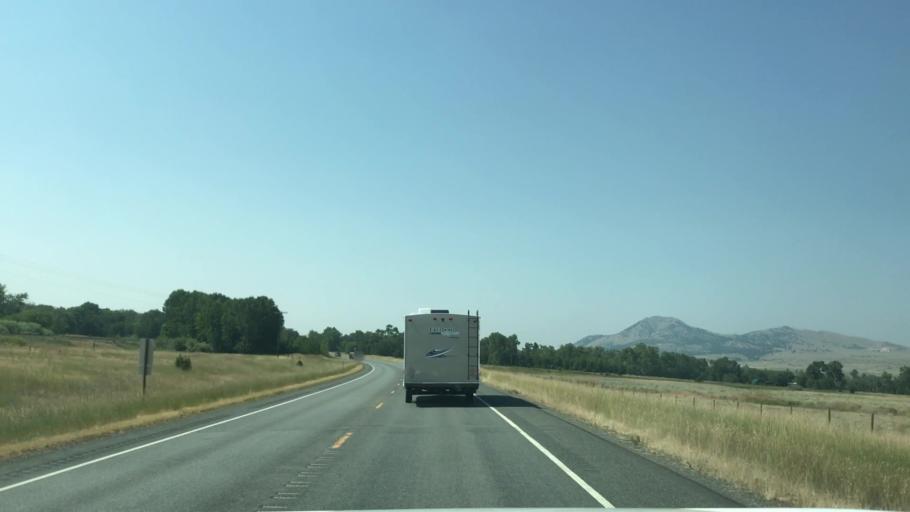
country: US
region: Montana
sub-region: Broadwater County
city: Townsend
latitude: 46.4828
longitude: -111.6639
